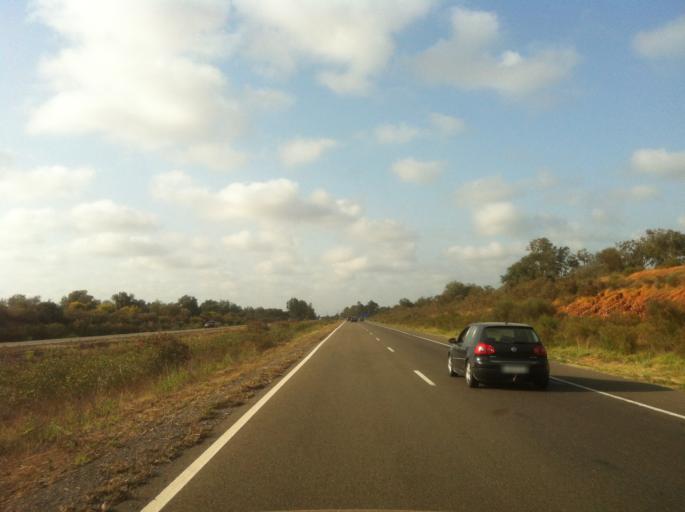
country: MA
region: Gharb-Chrarda-Beni Hssen
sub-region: Kenitra Province
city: Kenitra
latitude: 34.2247
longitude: -6.5483
